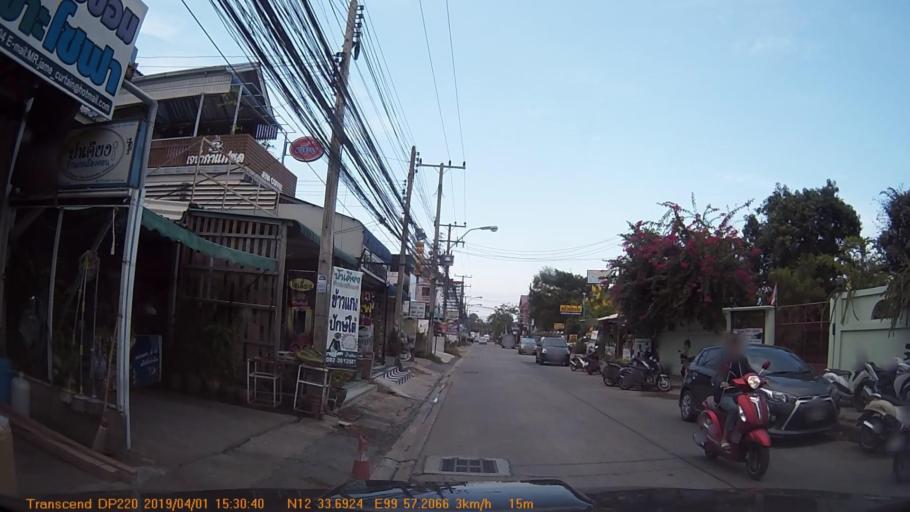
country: TH
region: Prachuap Khiri Khan
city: Hua Hin
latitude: 12.5616
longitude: 99.9536
